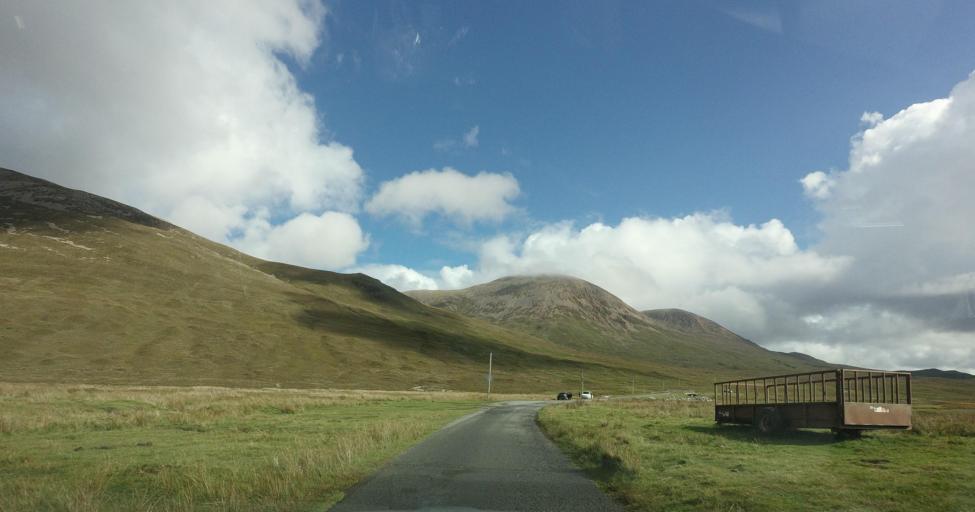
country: GB
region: Scotland
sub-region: Highland
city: Portree
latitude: 57.2279
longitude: -6.0401
